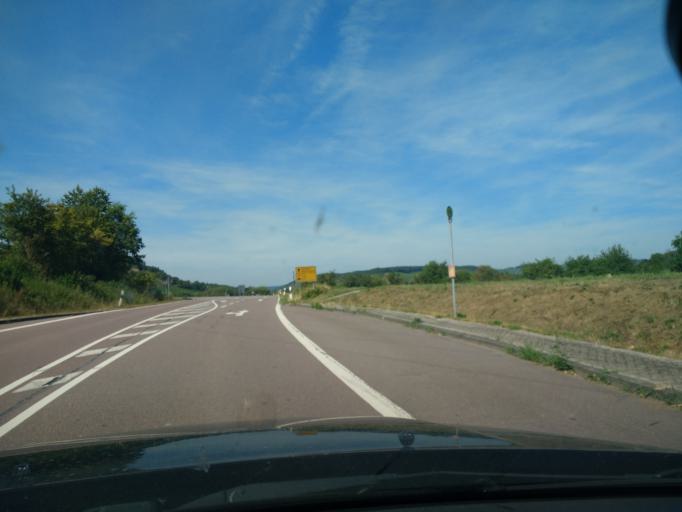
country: DE
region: Rheinland-Pfalz
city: Schoden
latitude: 49.6261
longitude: 6.5717
